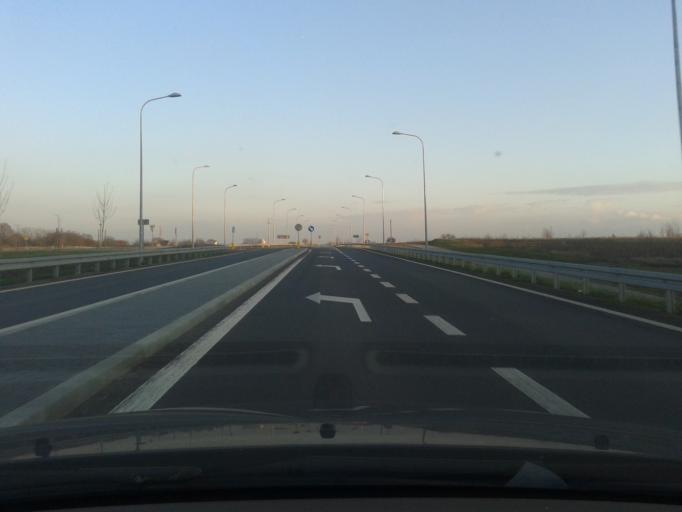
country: PL
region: Lublin Voivodeship
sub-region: Powiat opolski
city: Chodel
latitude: 51.1085
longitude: 22.0928
